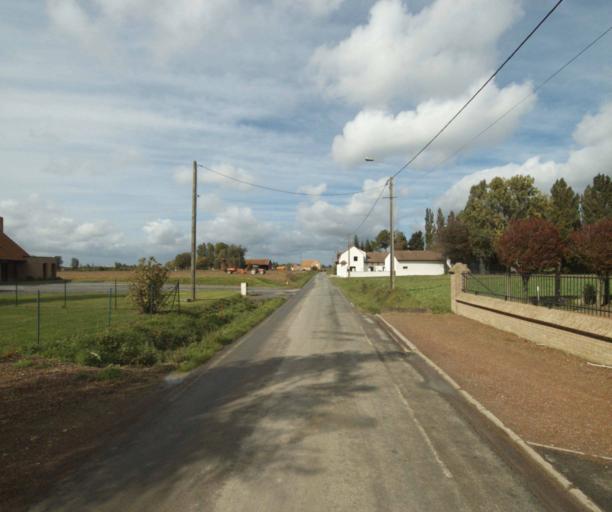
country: FR
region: Nord-Pas-de-Calais
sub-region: Departement du Nord
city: Houplines
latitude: 50.6813
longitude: 2.9330
